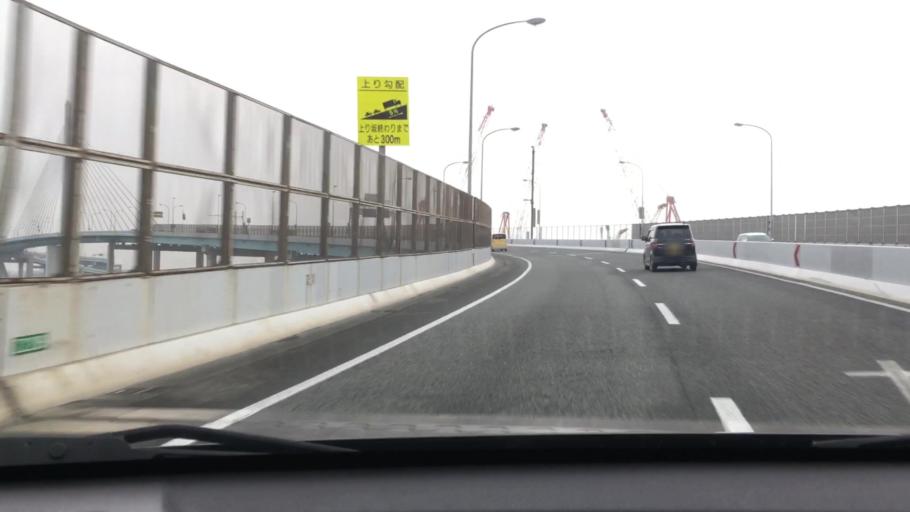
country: JP
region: Fukuoka
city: Fukuoka-shi
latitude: 33.5996
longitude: 130.3784
